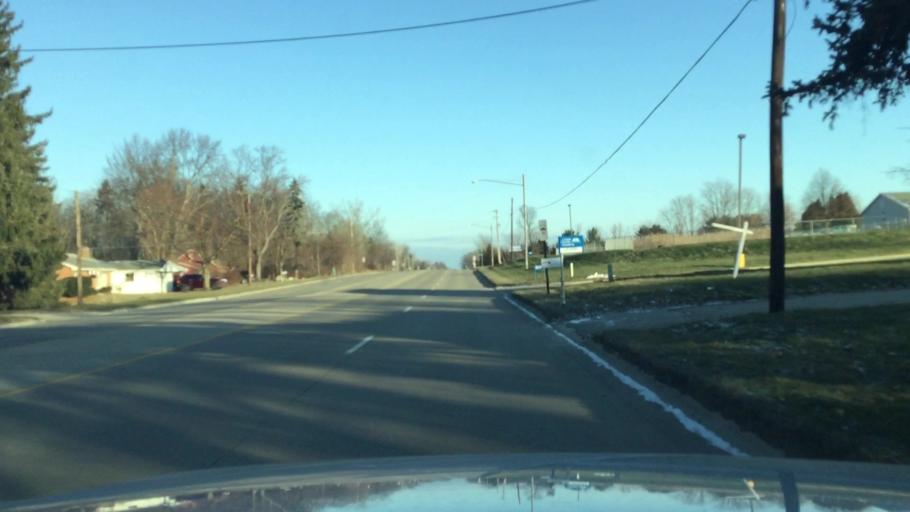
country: US
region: Michigan
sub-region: Genesee County
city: Flushing
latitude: 43.0515
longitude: -83.7727
